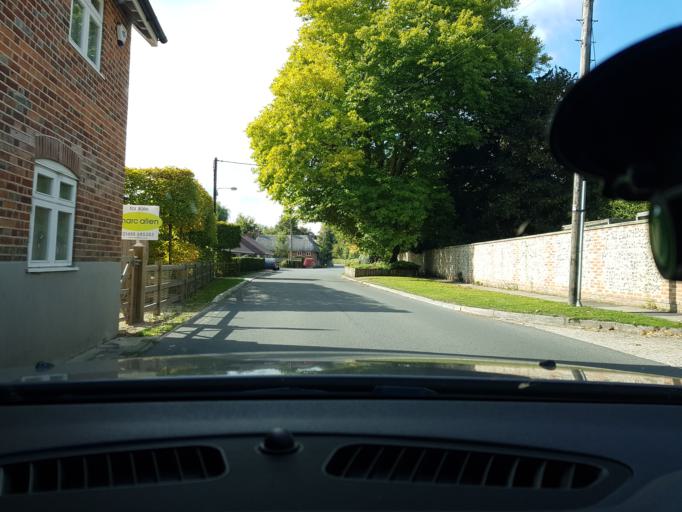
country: GB
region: England
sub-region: Wiltshire
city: Chilton Foliat
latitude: 51.4323
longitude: -1.5409
